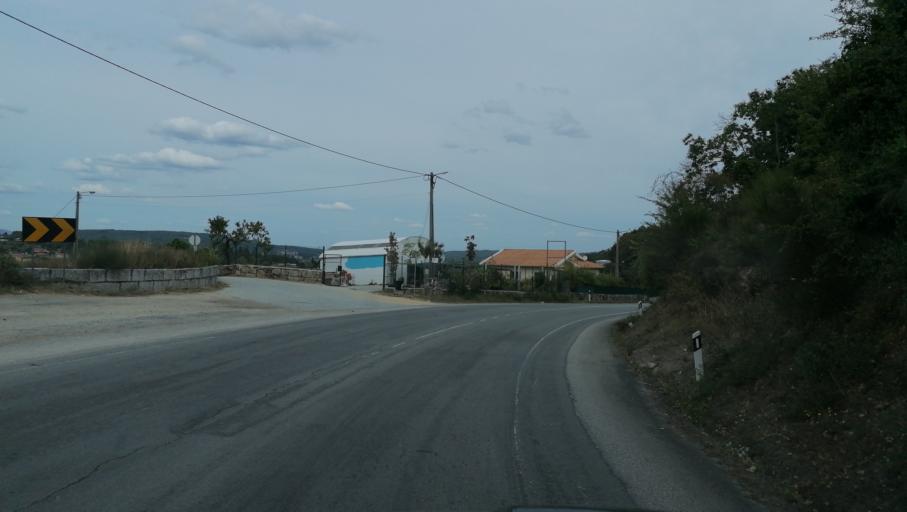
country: PT
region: Vila Real
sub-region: Vila Pouca de Aguiar
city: Vila Pouca de Aguiar
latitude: 41.5330
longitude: -7.6106
